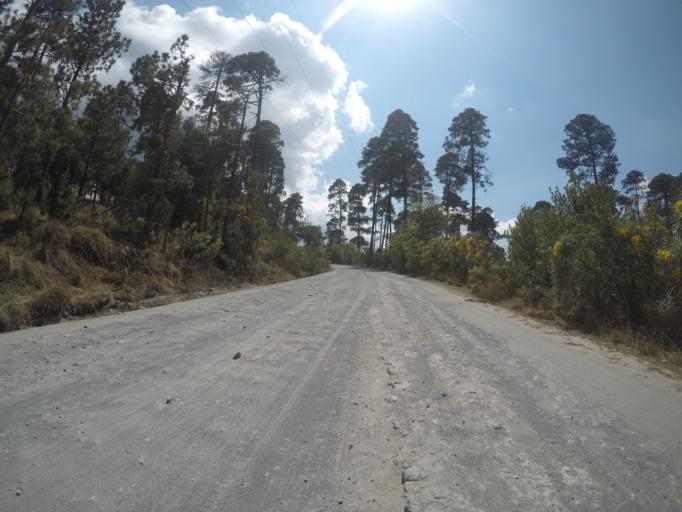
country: MX
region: Mexico
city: Cerro La Calera
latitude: 19.1469
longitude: -99.8036
